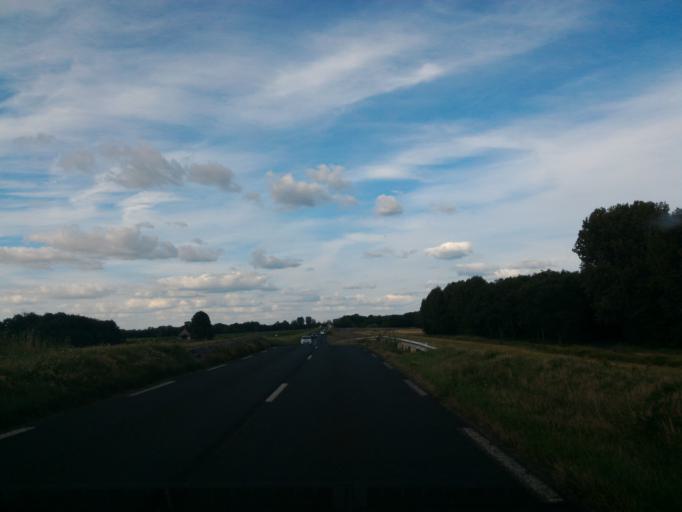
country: FR
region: Centre
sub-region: Departement du Loir-et-Cher
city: Montlivault
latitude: 47.6440
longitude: 1.4293
